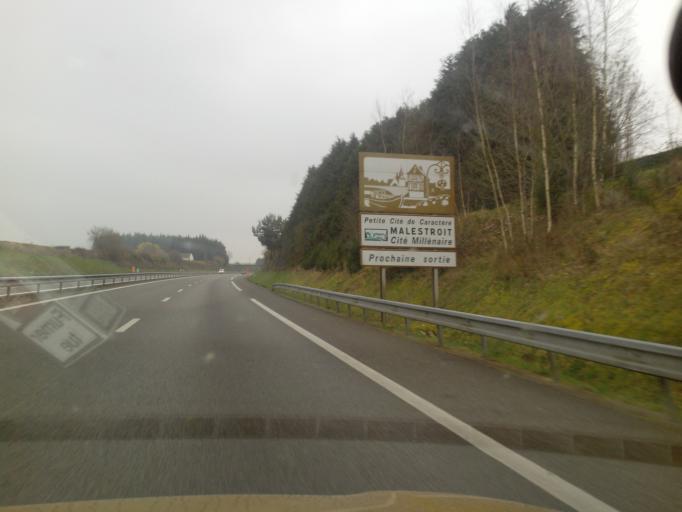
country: FR
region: Brittany
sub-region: Departement du Morbihan
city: Guillac
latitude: 47.8670
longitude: -2.4175
